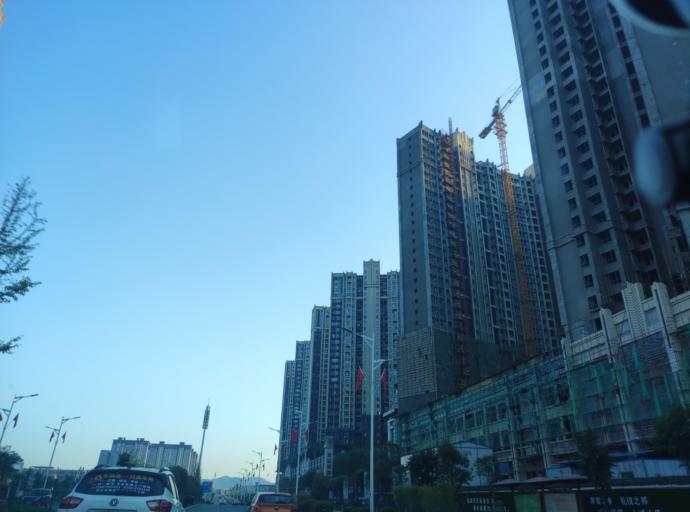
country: CN
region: Jiangxi Sheng
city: Pingxiang
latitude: 27.6346
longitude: 113.8296
